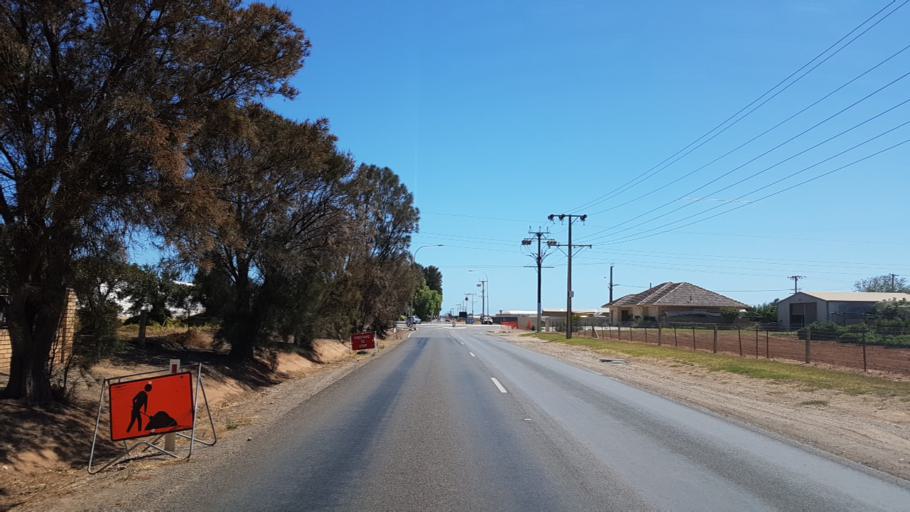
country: AU
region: South Australia
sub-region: Playford
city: Virginia
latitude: -34.7273
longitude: 138.5690
